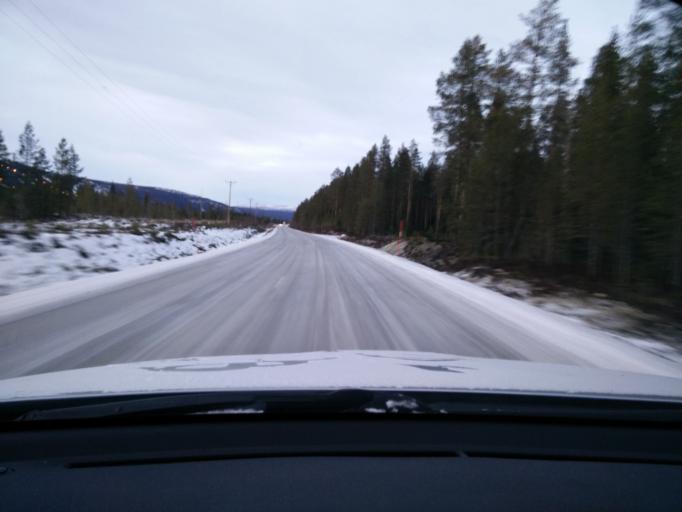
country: SE
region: Jaemtland
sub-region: Bergs Kommun
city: Hoverberg
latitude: 62.4880
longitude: 14.2271
